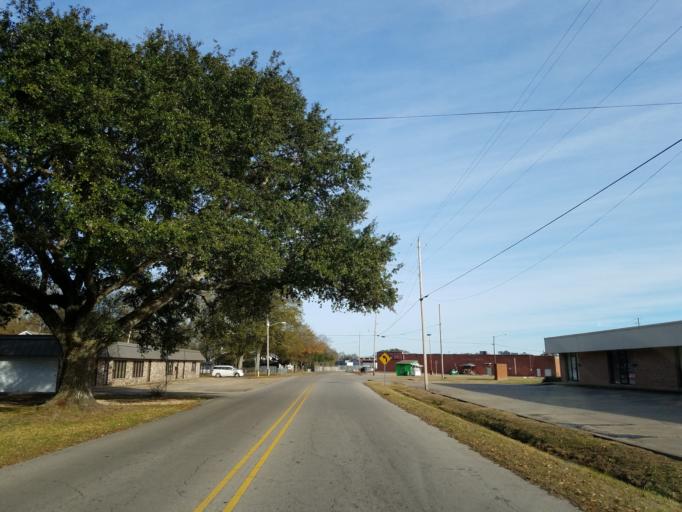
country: US
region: Mississippi
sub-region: Forrest County
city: Hattiesburg
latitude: 31.3174
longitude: -89.3079
